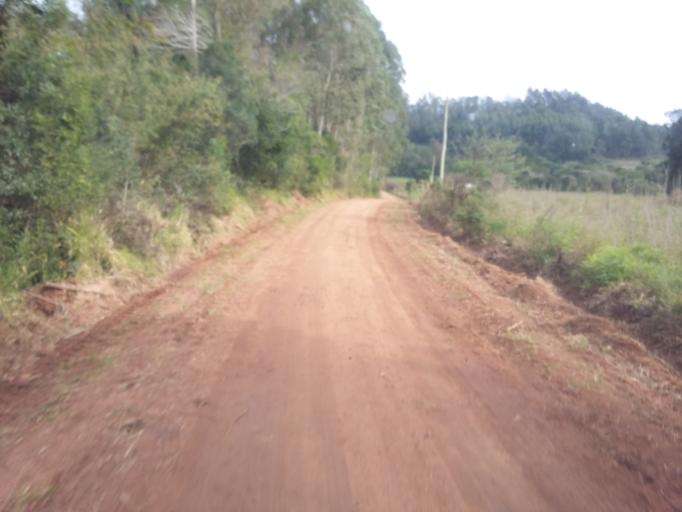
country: BR
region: Rio Grande do Sul
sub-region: Camaqua
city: Camaqua
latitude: -30.7112
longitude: -51.7725
